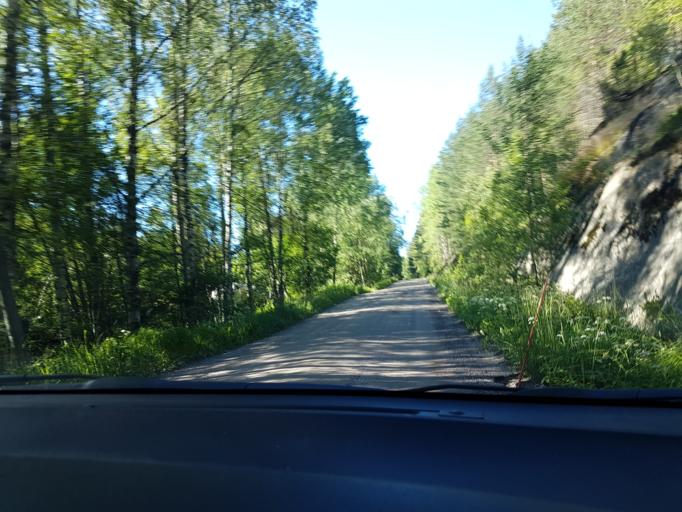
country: FI
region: Uusimaa
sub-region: Helsinki
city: Sibbo
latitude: 60.2760
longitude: 25.2349
